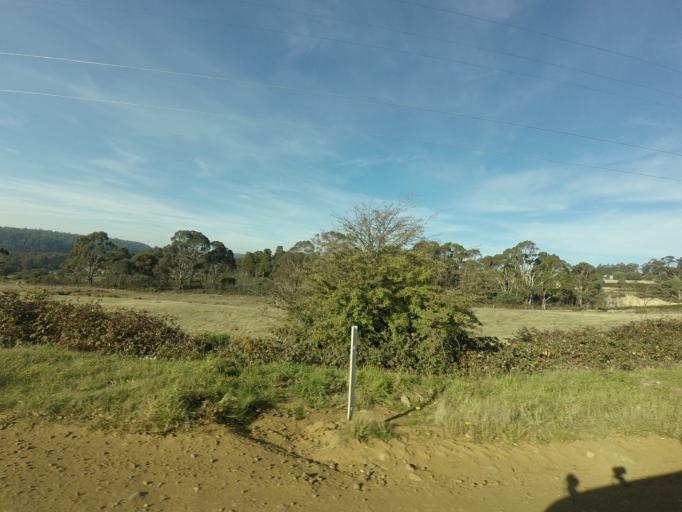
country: AU
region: Tasmania
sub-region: Brighton
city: Bridgewater
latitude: -42.4825
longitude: 147.3859
